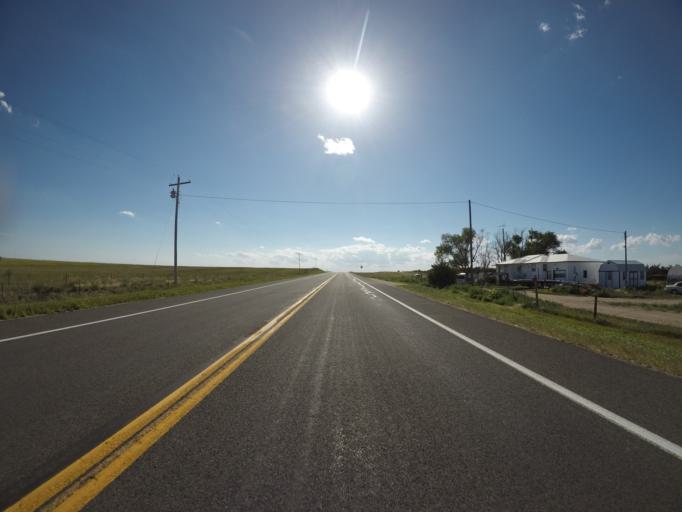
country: US
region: Colorado
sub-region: Morgan County
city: Brush
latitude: 40.6106
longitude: -103.6048
